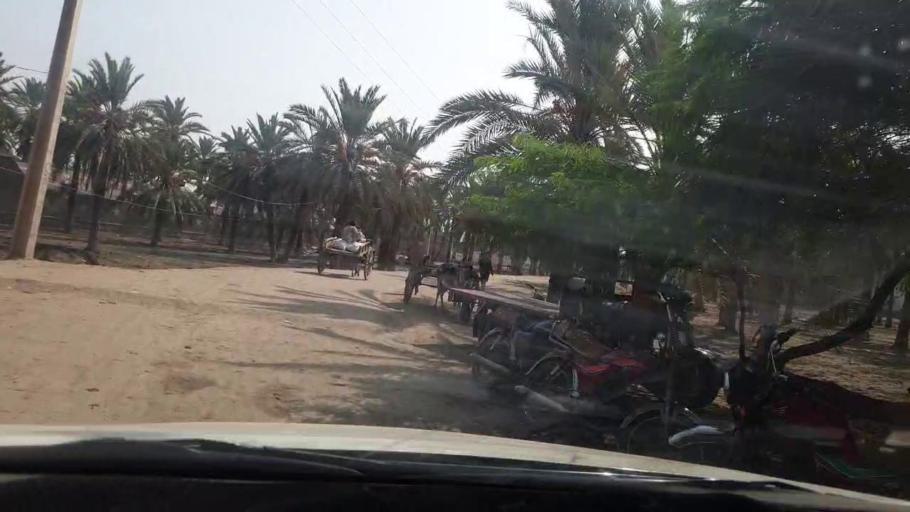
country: PK
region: Sindh
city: Rohri
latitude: 27.5952
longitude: 68.8829
